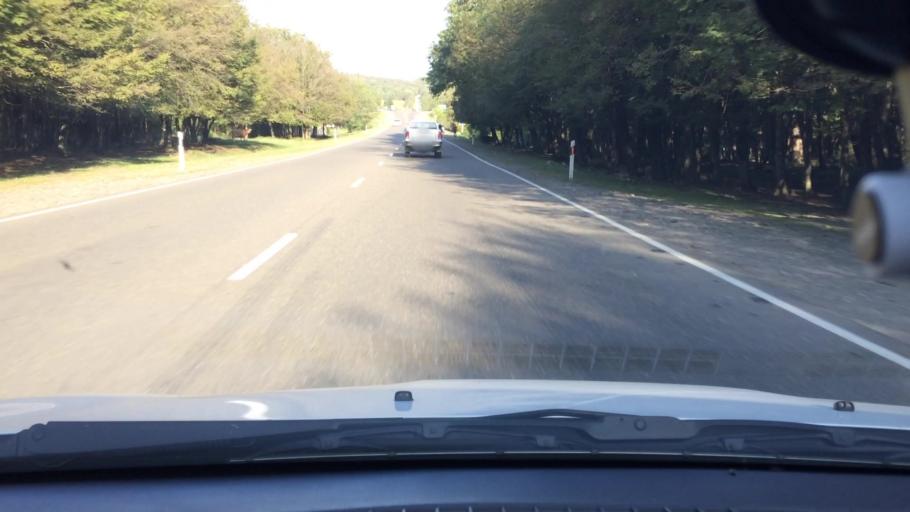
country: GE
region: Imereti
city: Kutaisi
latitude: 42.2359
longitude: 42.7710
